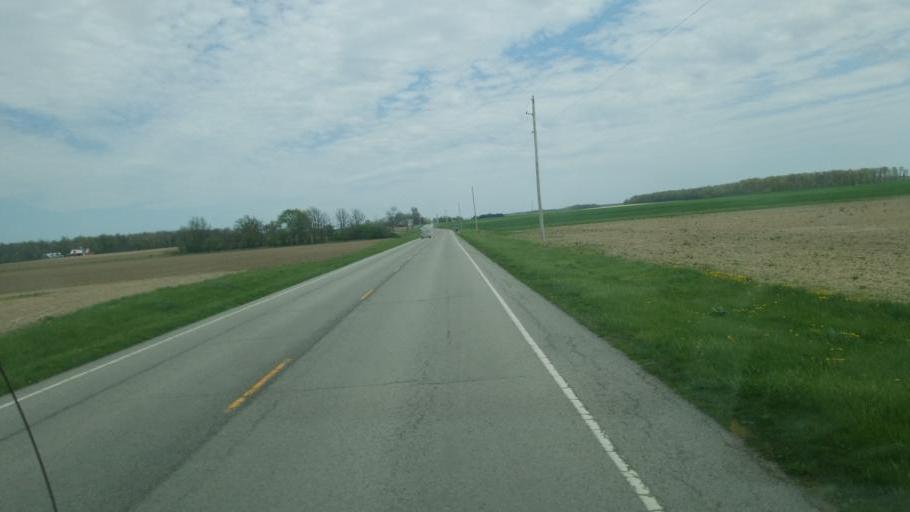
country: US
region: Ohio
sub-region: Hardin County
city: Ada
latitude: 40.8339
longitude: -83.7706
